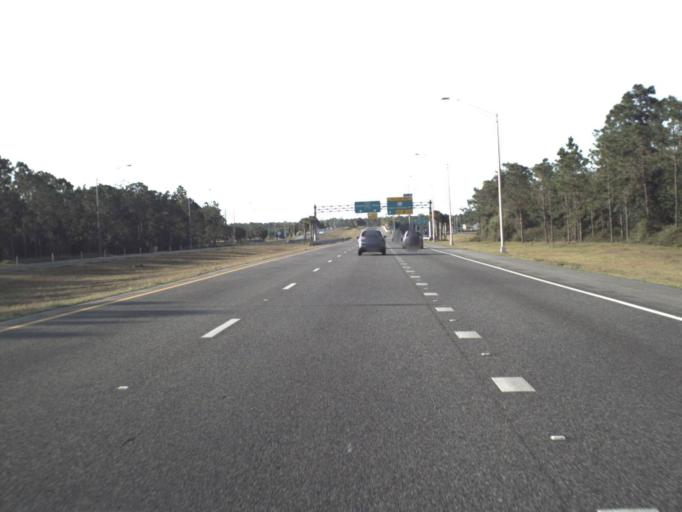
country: US
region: Florida
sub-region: Orange County
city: Alafaya
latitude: 28.5582
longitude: -81.1909
